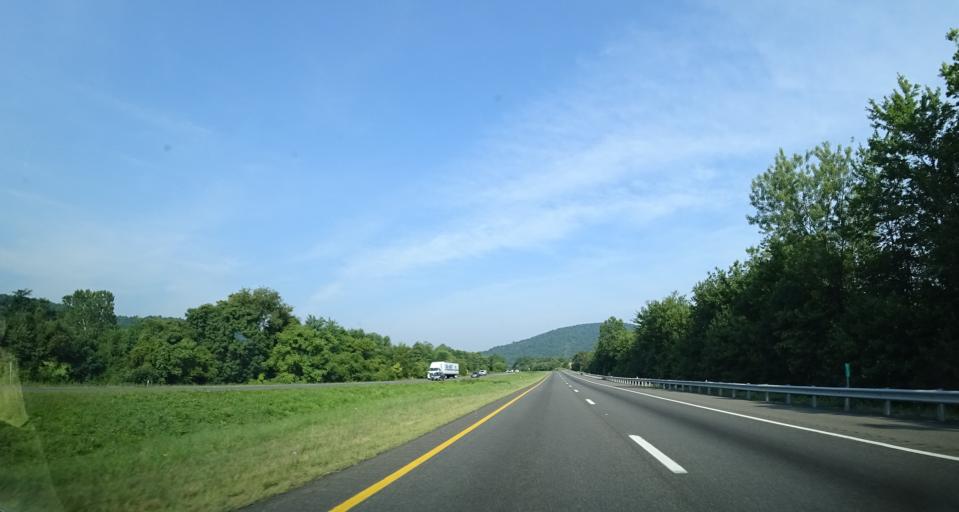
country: US
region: Virginia
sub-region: Fauquier County
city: Marshall
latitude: 38.9073
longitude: -77.9553
